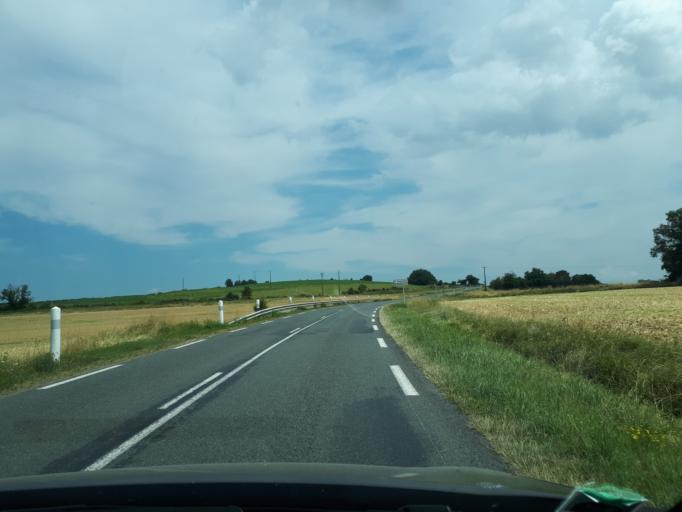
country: FR
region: Centre
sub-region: Departement du Cher
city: Rians
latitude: 47.2332
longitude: 2.6428
